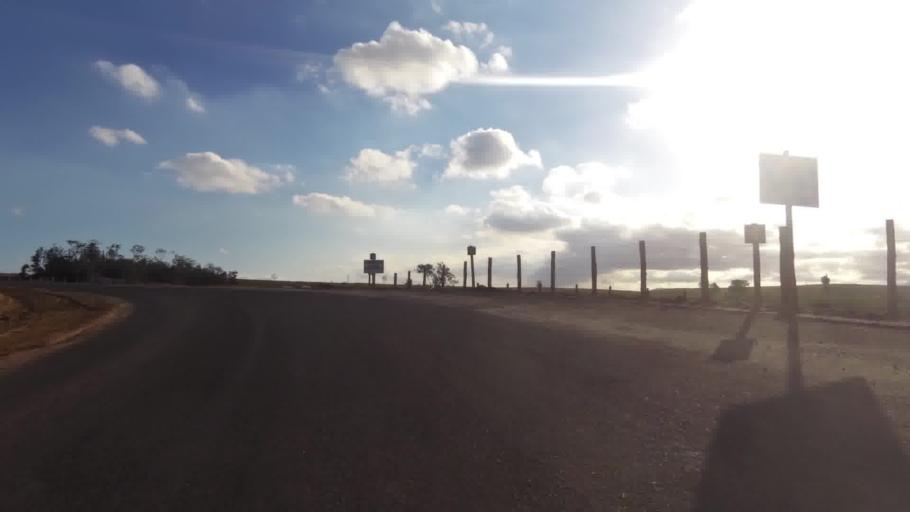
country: BR
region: Espirito Santo
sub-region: Marataizes
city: Marataizes
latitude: -21.1369
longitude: -41.0579
